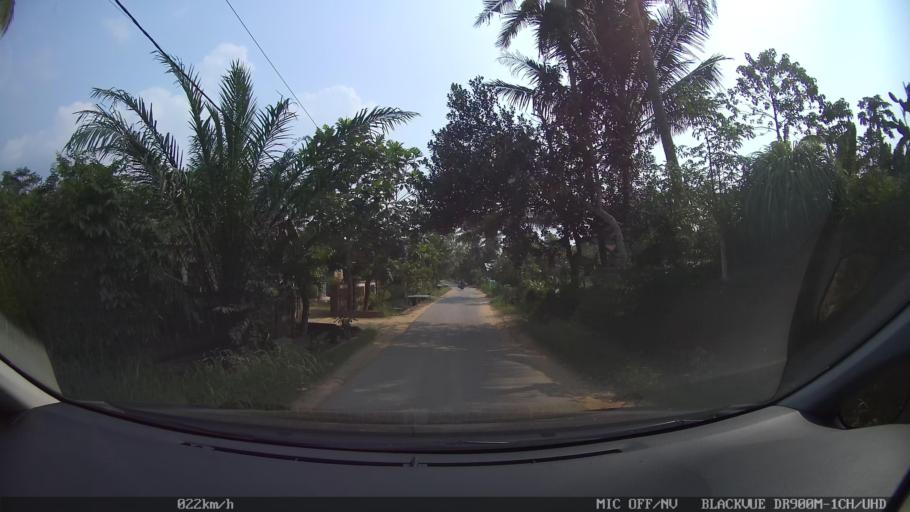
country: ID
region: Lampung
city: Pringsewu
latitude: -5.3922
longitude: 104.9934
